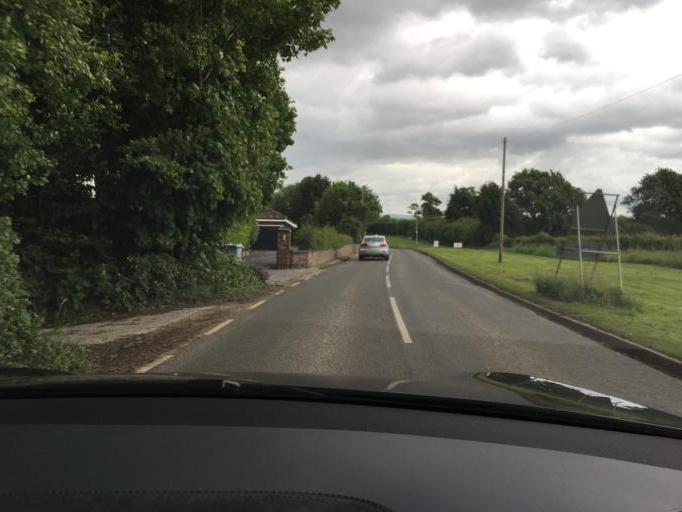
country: GB
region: England
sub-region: Cheshire East
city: Poynton
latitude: 53.3593
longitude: -2.1347
